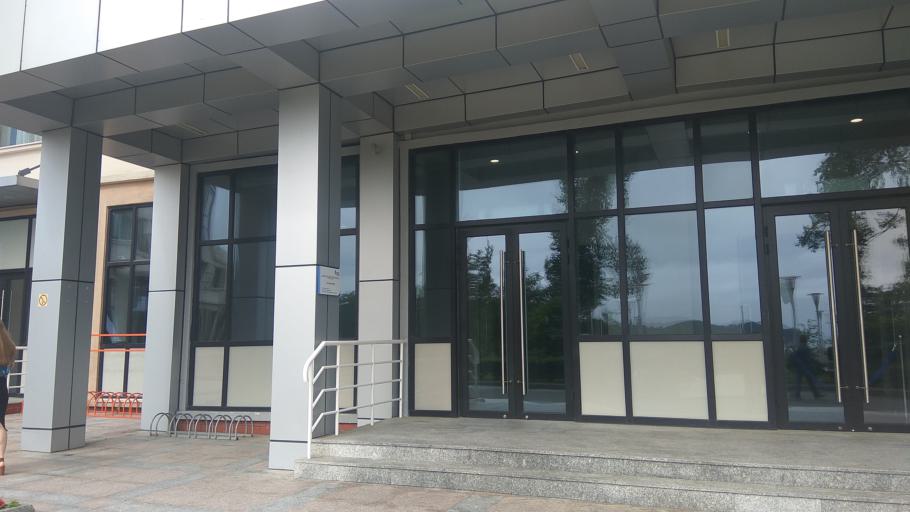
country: RU
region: Primorskiy
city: Russkiy
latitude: 43.0292
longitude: 131.8884
